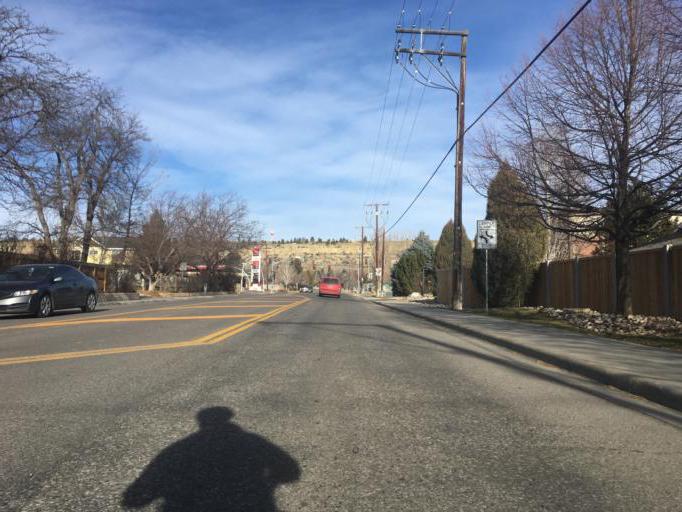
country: US
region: Montana
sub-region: Yellowstone County
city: Billings
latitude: 45.7938
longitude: -108.5590
